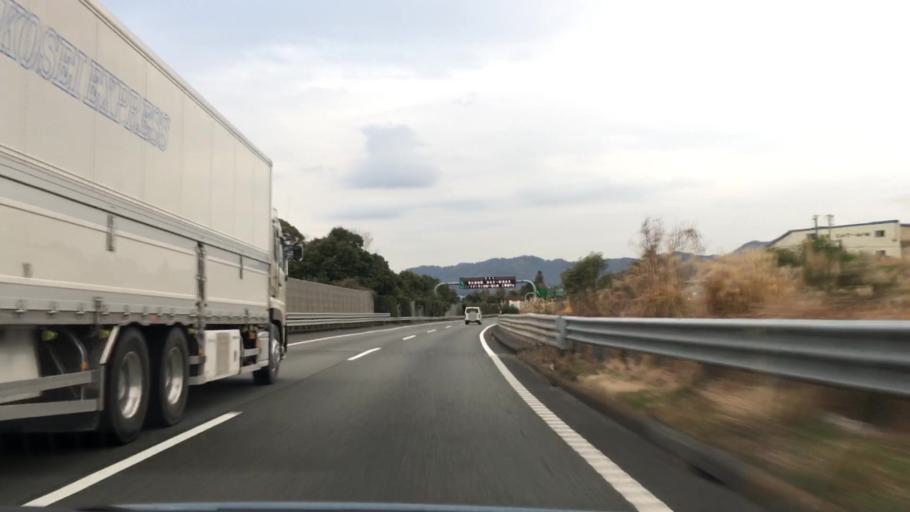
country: JP
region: Shizuoka
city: Shizuoka-shi
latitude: 35.0477
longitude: 138.4958
